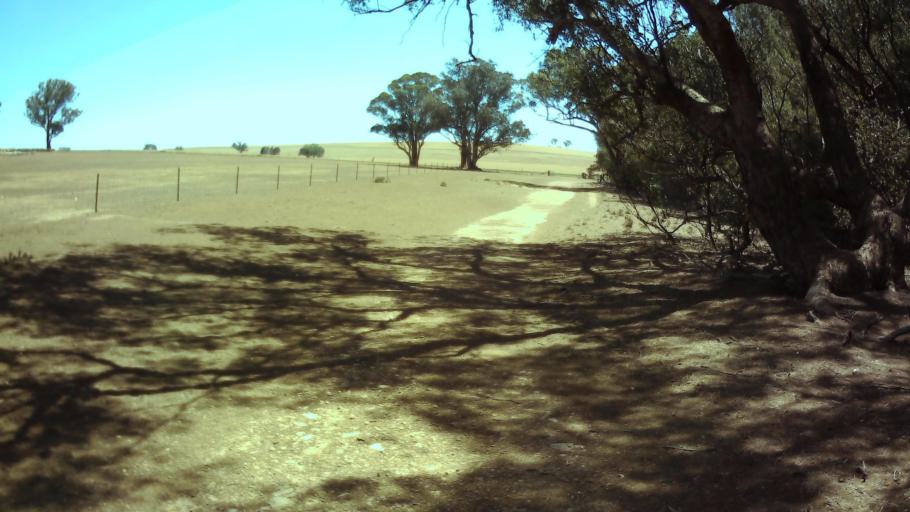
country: AU
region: New South Wales
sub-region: Weddin
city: Grenfell
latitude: -33.9834
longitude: 148.1642
